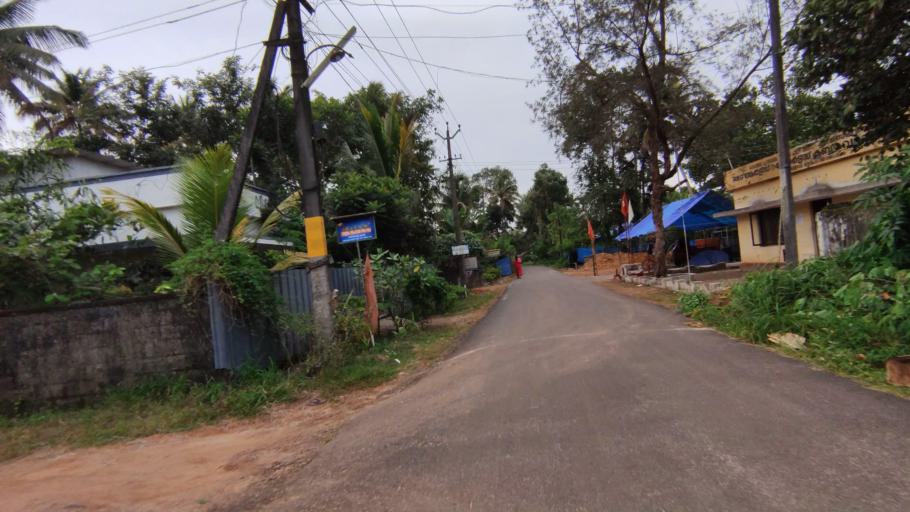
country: IN
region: Kerala
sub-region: Alappuzha
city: Shertallai
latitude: 9.6272
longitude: 76.3572
